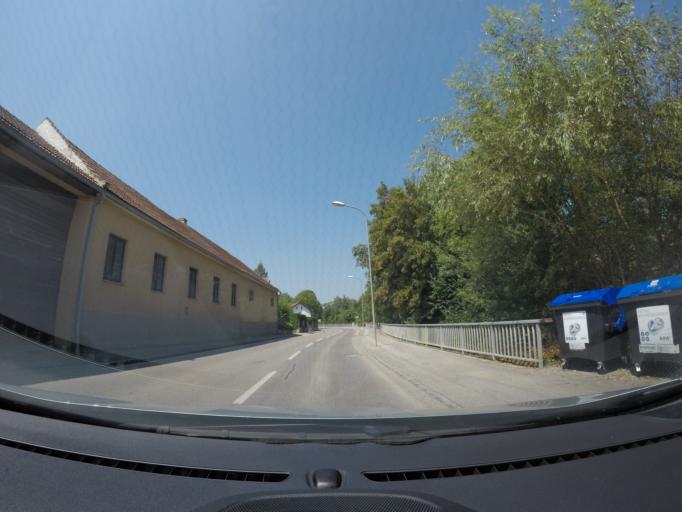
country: AT
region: Lower Austria
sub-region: Politischer Bezirk Sankt Polten
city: Eichgraben
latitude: 48.1842
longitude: 15.9627
